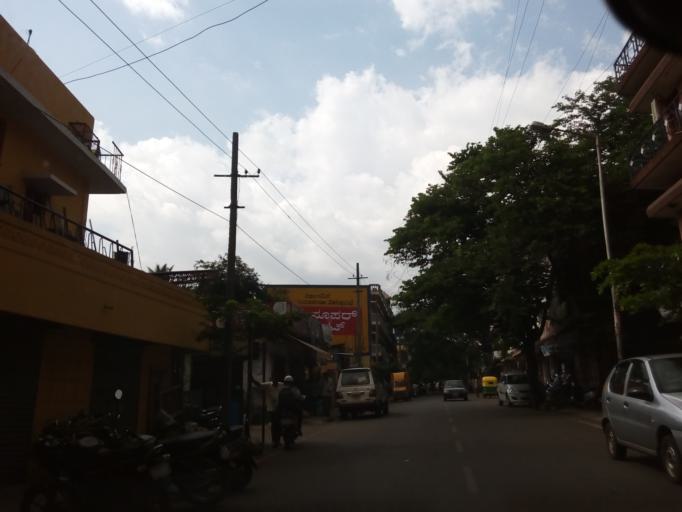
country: IN
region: Karnataka
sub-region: Bangalore Urban
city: Bangalore
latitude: 13.0254
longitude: 77.5602
